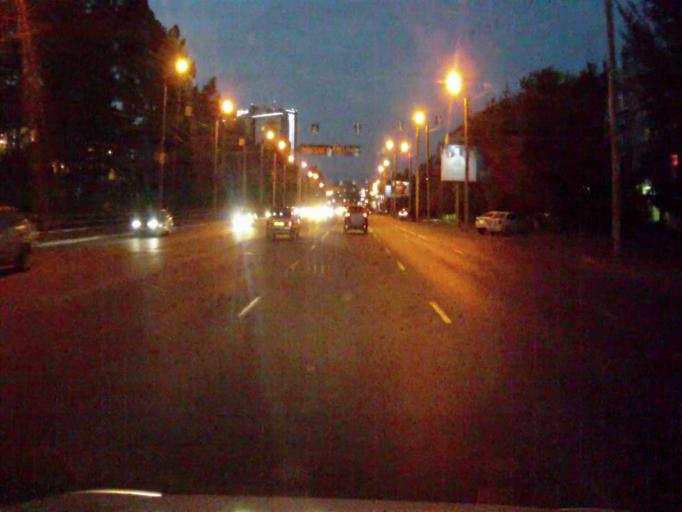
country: RU
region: Chelyabinsk
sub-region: Gorod Chelyabinsk
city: Chelyabinsk
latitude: 55.1638
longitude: 61.3810
